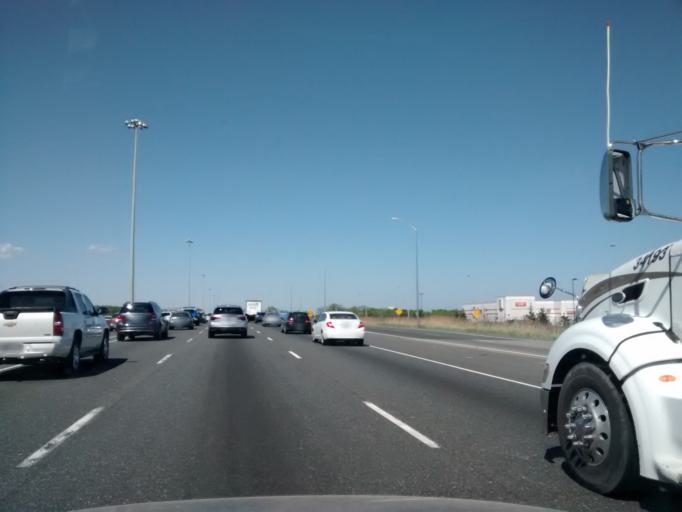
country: CA
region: Ontario
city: Oakville
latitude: 43.3992
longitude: -79.7520
